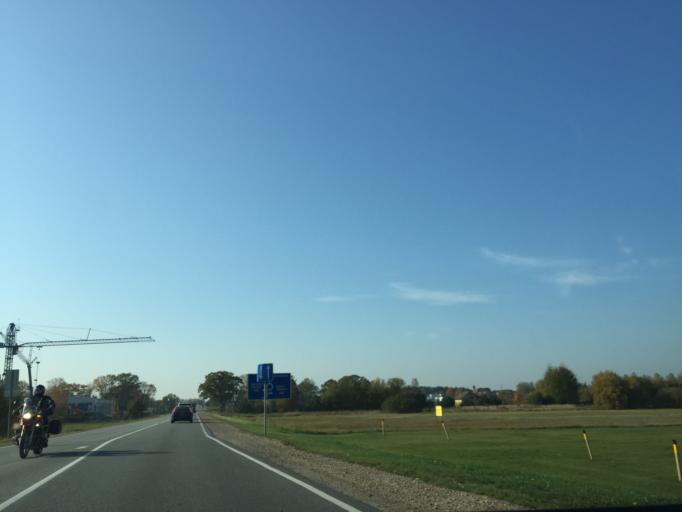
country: LV
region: Babite
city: Pinki
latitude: 56.8801
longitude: 23.9622
